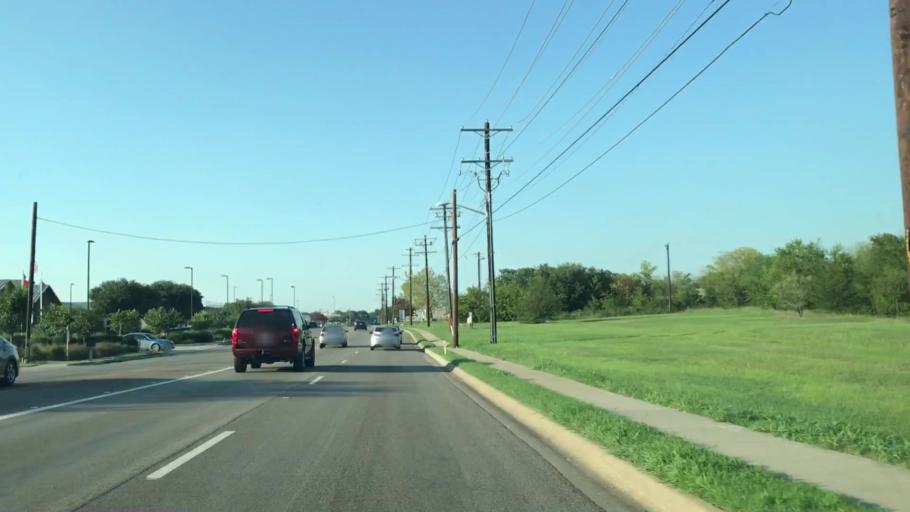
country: US
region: Texas
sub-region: Denton County
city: Denton
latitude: 33.2105
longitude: -97.1119
